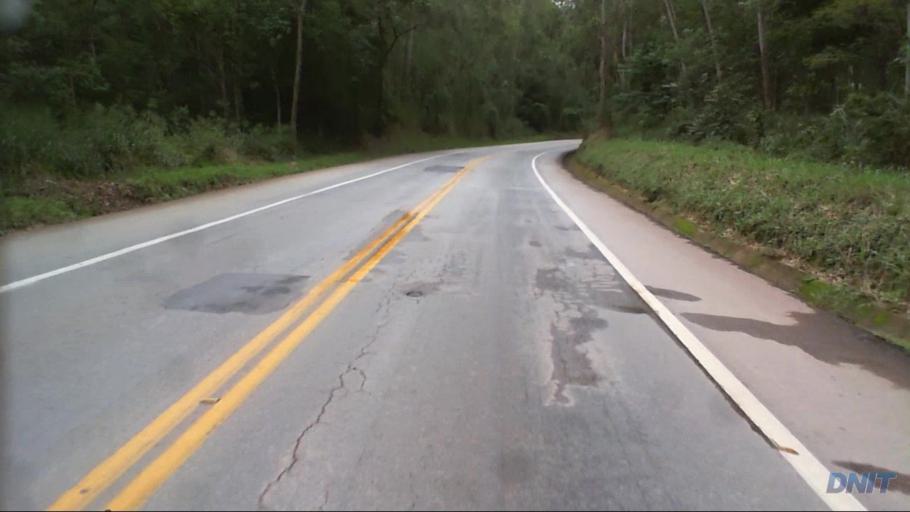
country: BR
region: Minas Gerais
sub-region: Joao Monlevade
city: Joao Monlevade
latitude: -19.8524
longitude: -43.1406
